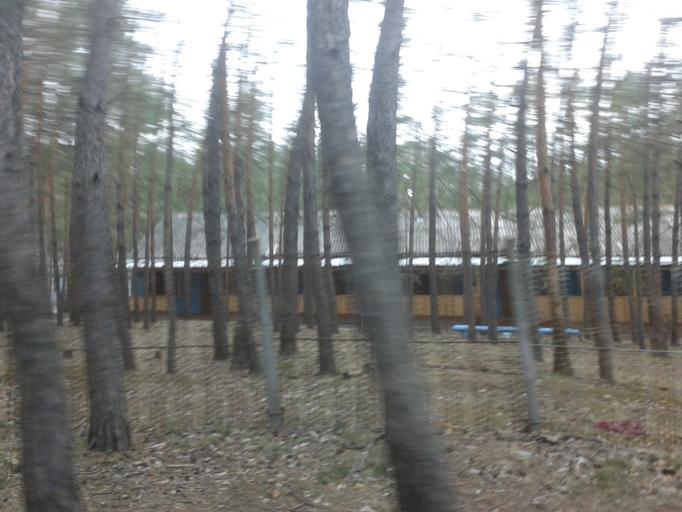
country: RU
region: Rjazan
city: Solotcha
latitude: 54.7798
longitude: 39.7944
